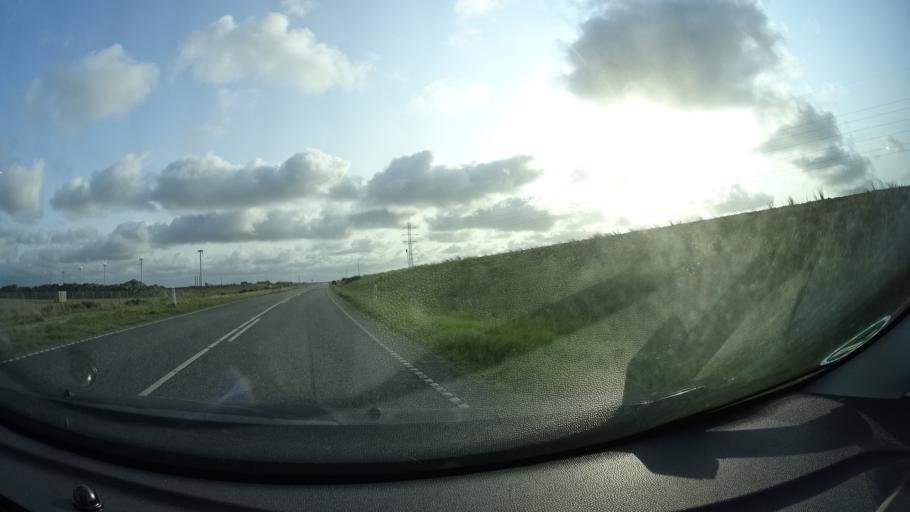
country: DK
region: Central Jutland
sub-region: Lemvig Kommune
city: Thyboron
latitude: 56.6783
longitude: 8.2221
